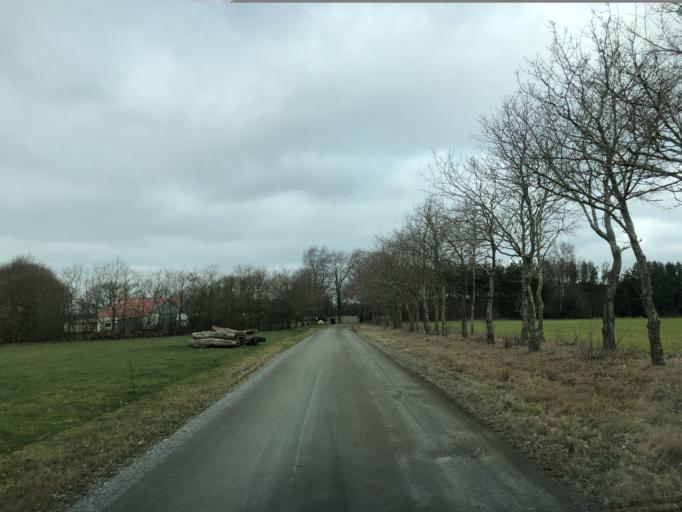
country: DK
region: South Denmark
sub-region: Billund Kommune
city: Billund
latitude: 55.7731
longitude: 9.1397
